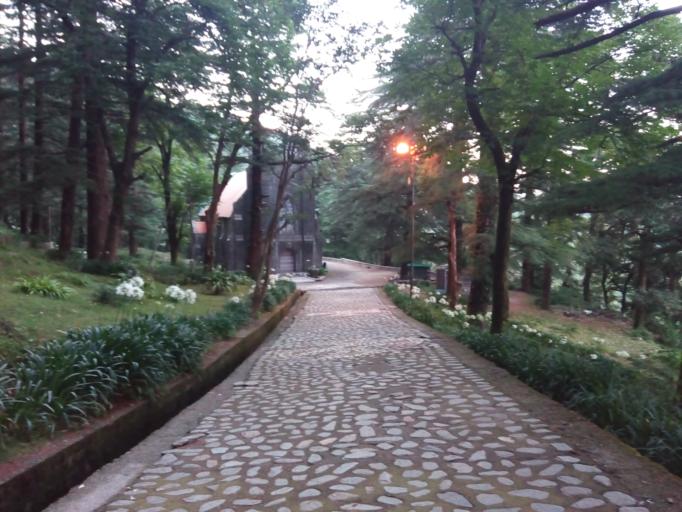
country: IN
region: Himachal Pradesh
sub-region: Kangra
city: Dharmsala
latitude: 32.2430
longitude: 76.3177
